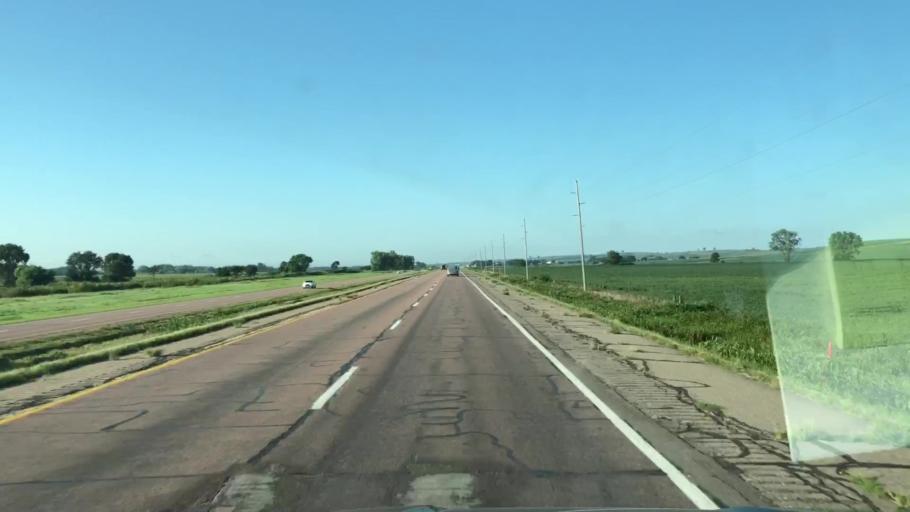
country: US
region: Iowa
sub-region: Plymouth County
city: Le Mars
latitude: 42.6897
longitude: -96.2638
